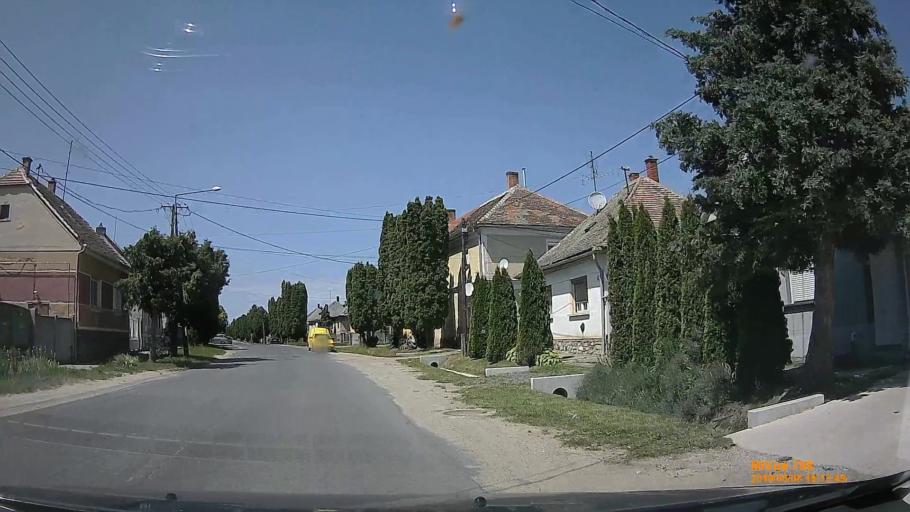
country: HU
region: Vas
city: Csepreg
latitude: 47.3959
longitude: 16.7106
